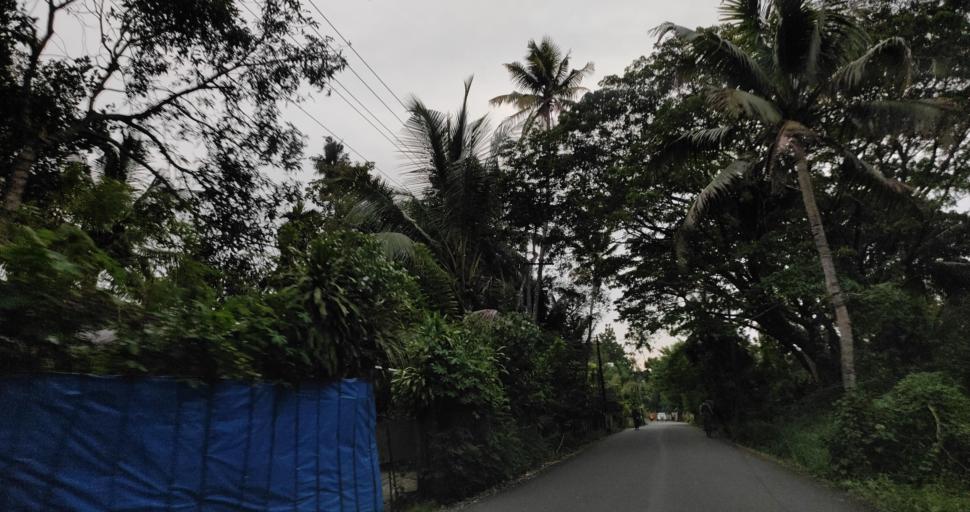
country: IN
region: Kerala
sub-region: Alappuzha
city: Vayalar
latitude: 9.6874
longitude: 76.3298
